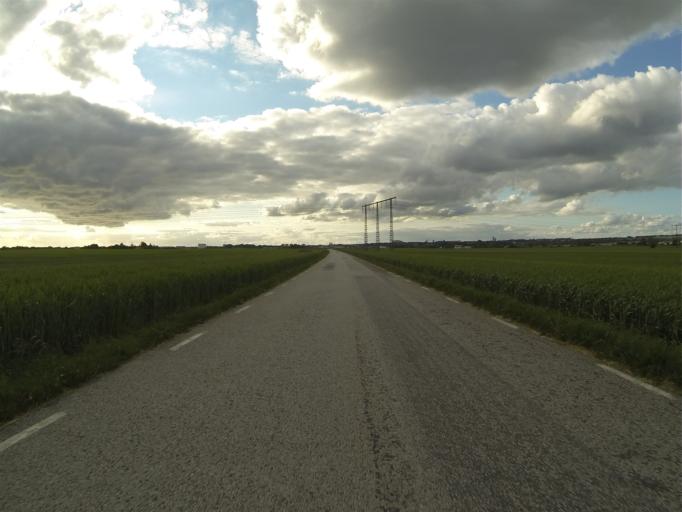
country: SE
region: Skane
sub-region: Staffanstorps Kommun
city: Staffanstorp
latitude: 55.6747
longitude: 13.2321
